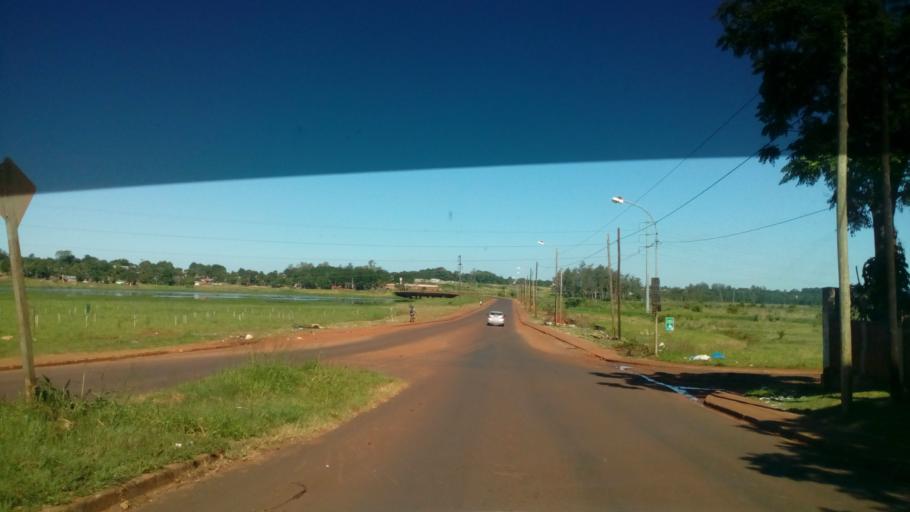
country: AR
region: Misiones
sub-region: Departamento de Capital
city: Posadas
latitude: -27.4284
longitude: -55.9085
